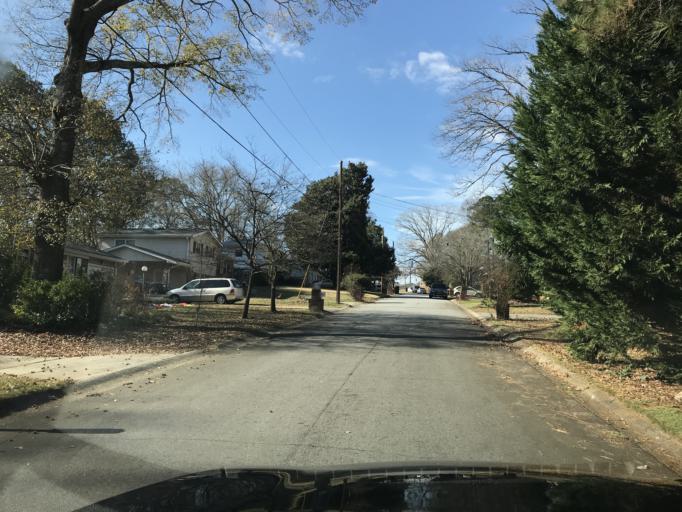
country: US
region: Georgia
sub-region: Clayton County
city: Morrow
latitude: 33.5815
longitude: -84.3713
